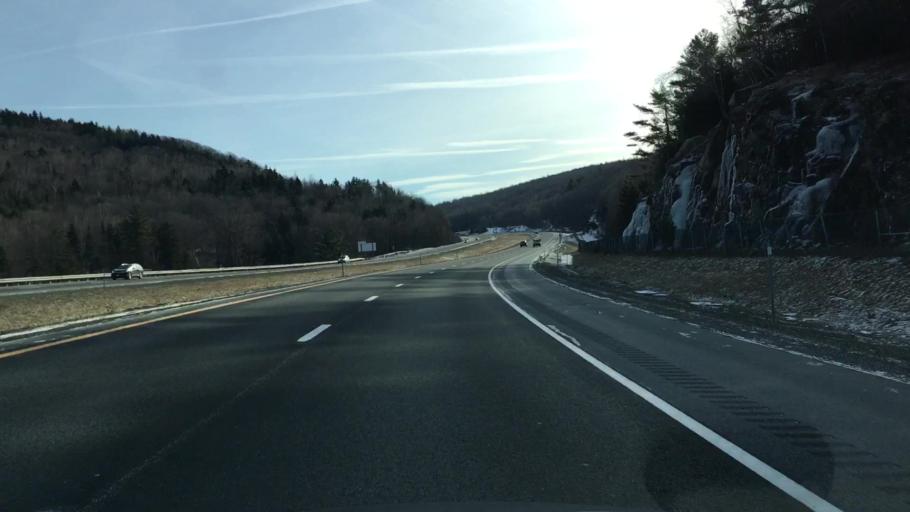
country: US
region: New Hampshire
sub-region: Grafton County
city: Enfield
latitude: 43.5807
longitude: -72.1619
